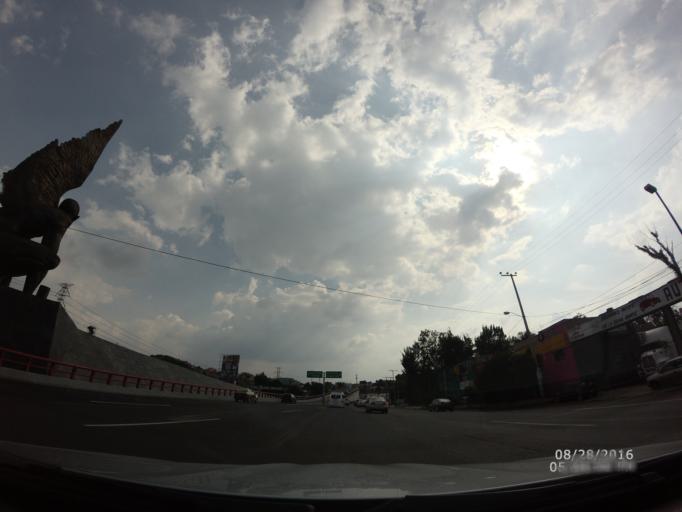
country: MX
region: Mexico
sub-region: Tlalnepantla de Baz
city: Puerto Escondido (Tepeolulco Puerto Escondido)
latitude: 19.5232
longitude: -99.0899
